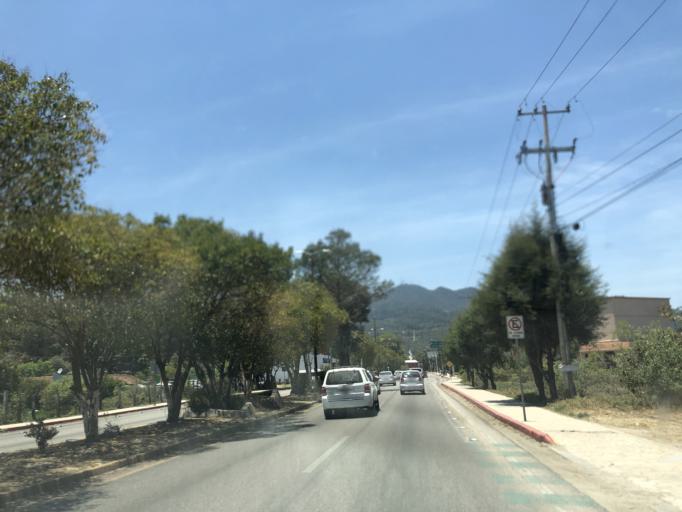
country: MX
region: Chiapas
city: San Cristobal de las Casas
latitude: 16.7320
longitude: -92.6498
